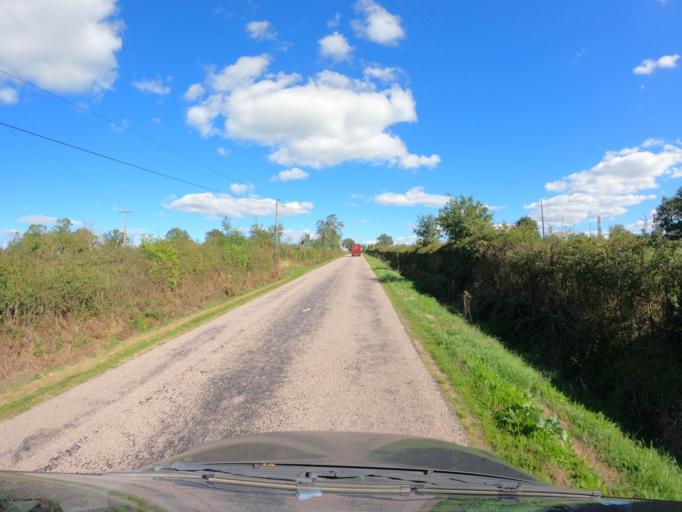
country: FR
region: Auvergne
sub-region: Departement de l'Allier
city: Buxieres-les-Mines
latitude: 46.4043
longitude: 3.0074
